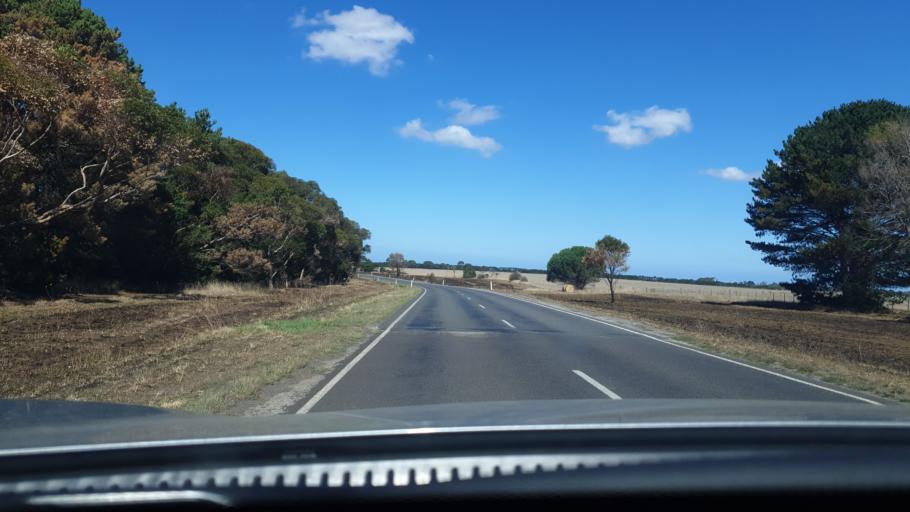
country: AU
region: Victoria
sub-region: Warrnambool
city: Warrnambool
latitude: -38.1661
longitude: 142.3976
